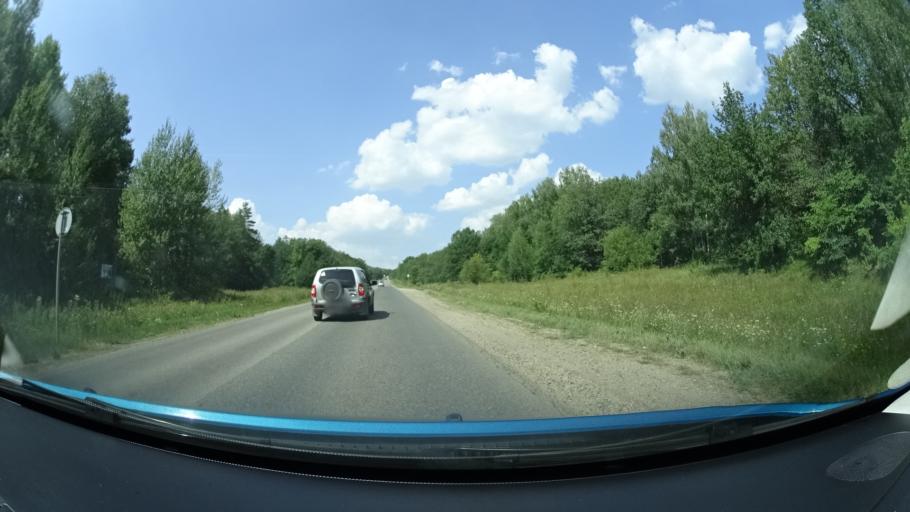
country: RU
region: Bashkortostan
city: Oktyabr'skiy
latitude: 54.4555
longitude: 53.5868
